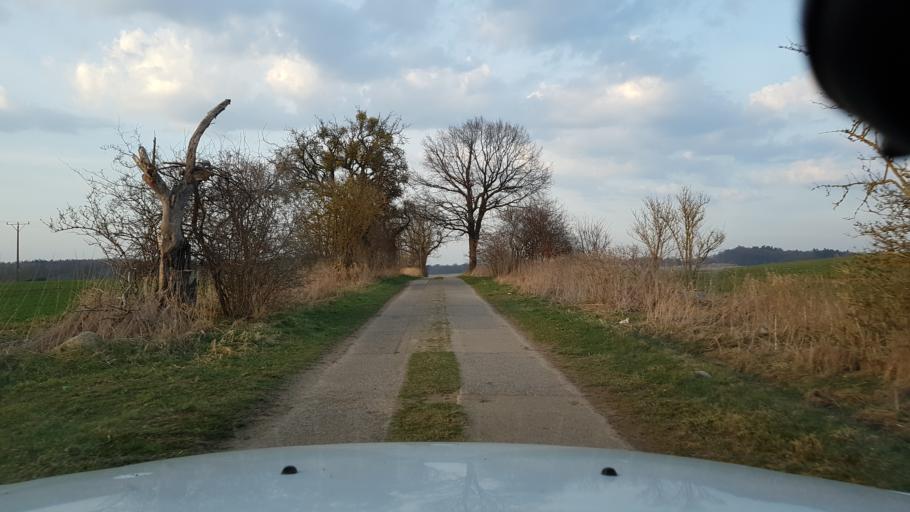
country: PL
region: West Pomeranian Voivodeship
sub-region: Koszalin
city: Koszalin
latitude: 54.0928
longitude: 16.1365
